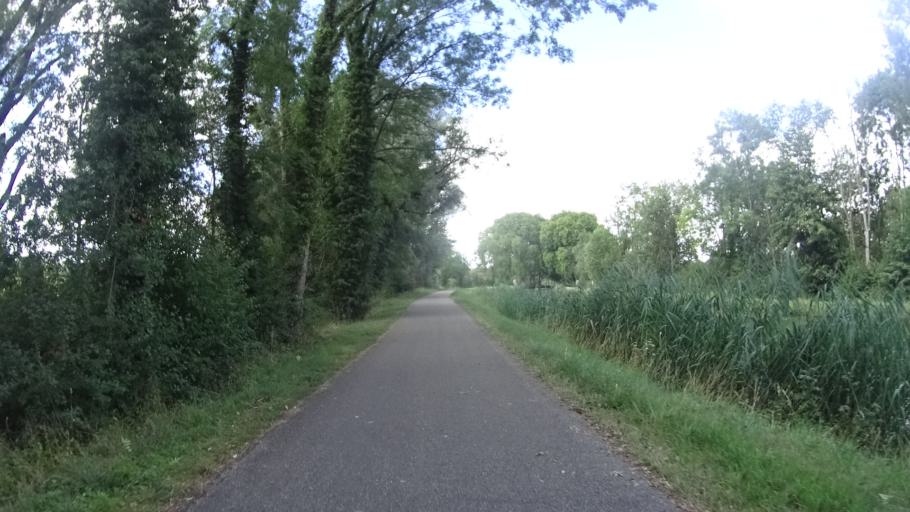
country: FR
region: Franche-Comte
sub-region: Departement du Jura
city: Dole
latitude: 47.0931
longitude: 5.5166
